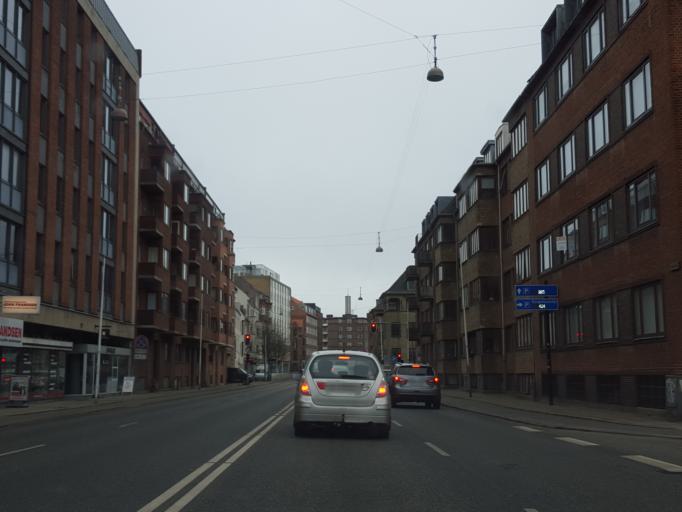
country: DK
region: North Denmark
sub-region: Alborg Kommune
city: Aalborg
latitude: 57.0438
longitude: 9.9116
